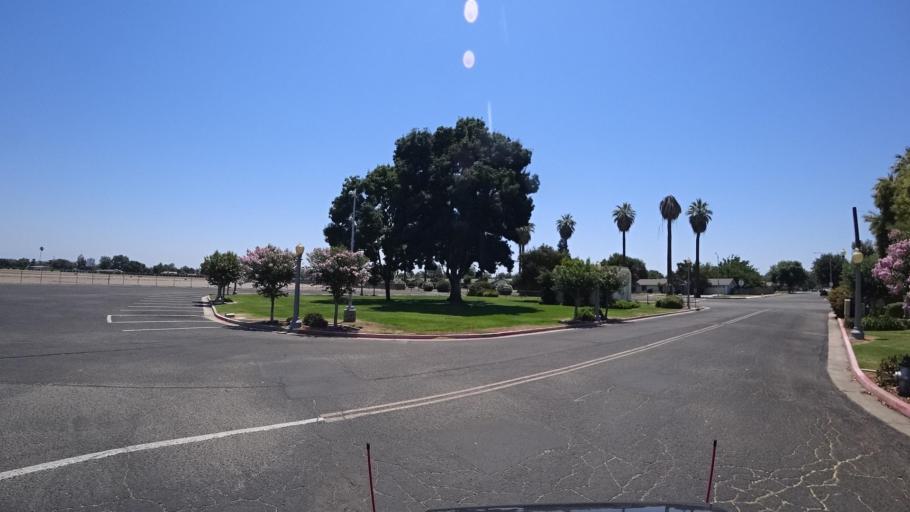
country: US
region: California
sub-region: Fresno County
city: West Park
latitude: 36.7291
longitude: -119.8177
